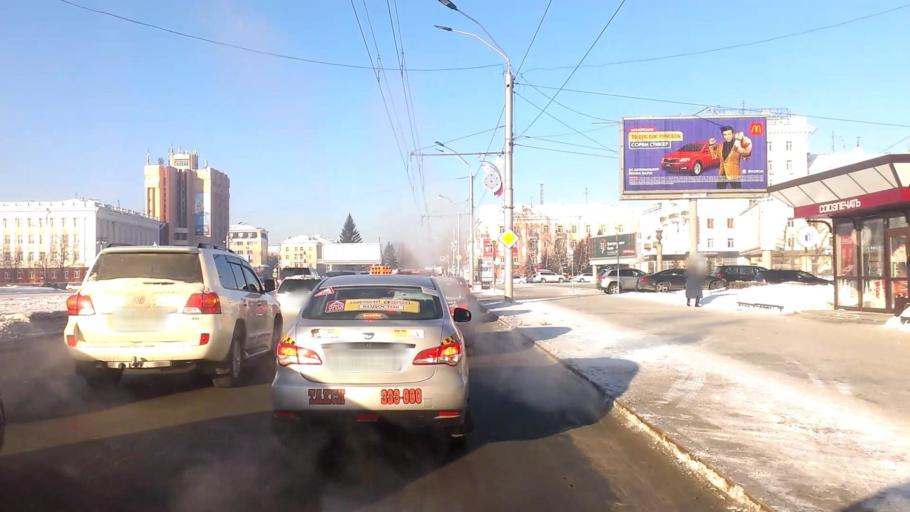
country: RU
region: Altai Krai
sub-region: Gorod Barnaulskiy
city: Barnaul
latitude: 53.3466
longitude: 83.7788
